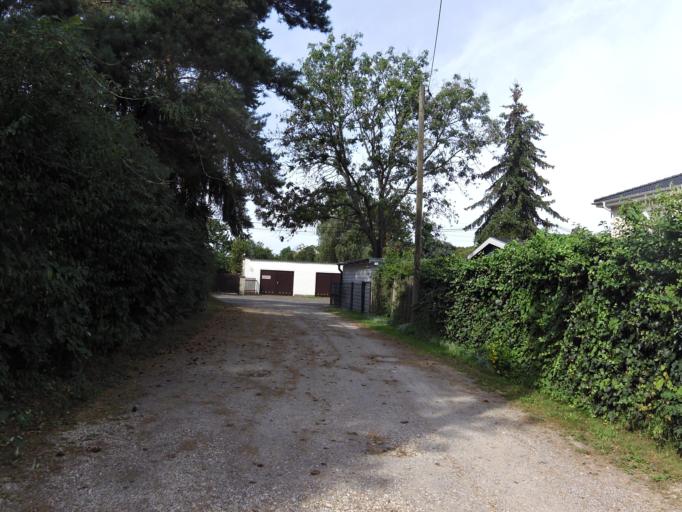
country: DE
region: Saxony
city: Schkeuditz
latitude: 51.3621
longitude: 12.2810
